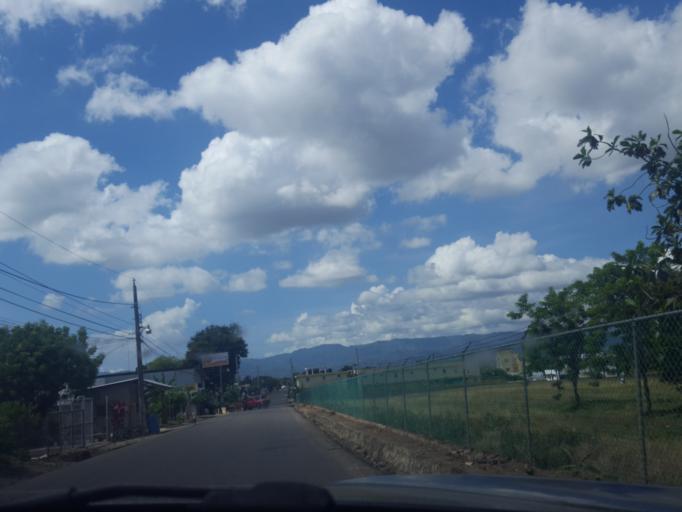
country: DO
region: Santiago
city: Licey al Medio
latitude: 19.3891
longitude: -70.6493
